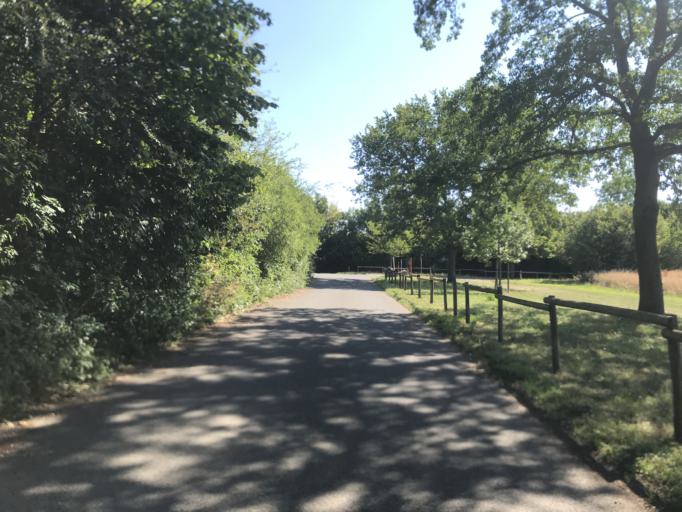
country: DE
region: Rheinland-Pfalz
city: Ockenheim
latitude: 49.9355
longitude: 7.9883
